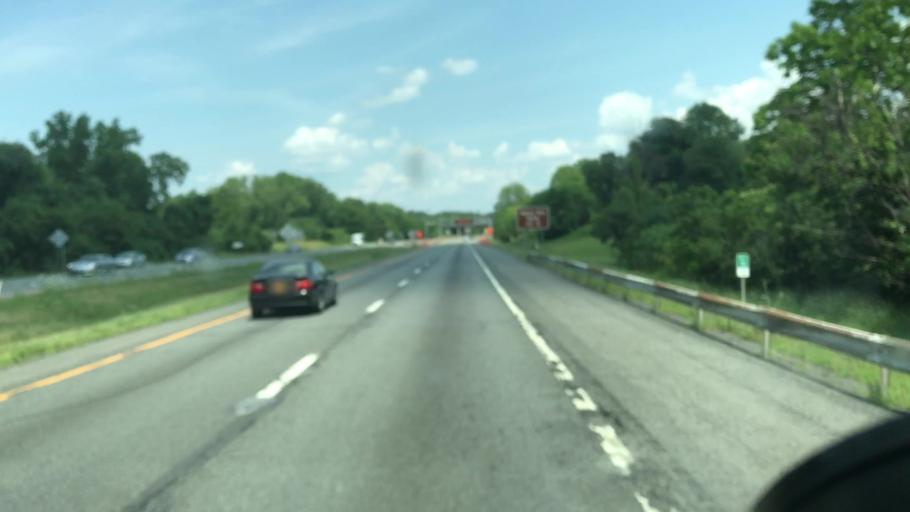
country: US
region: New York
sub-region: Orange County
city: Balmville
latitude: 41.5177
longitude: -74.0362
